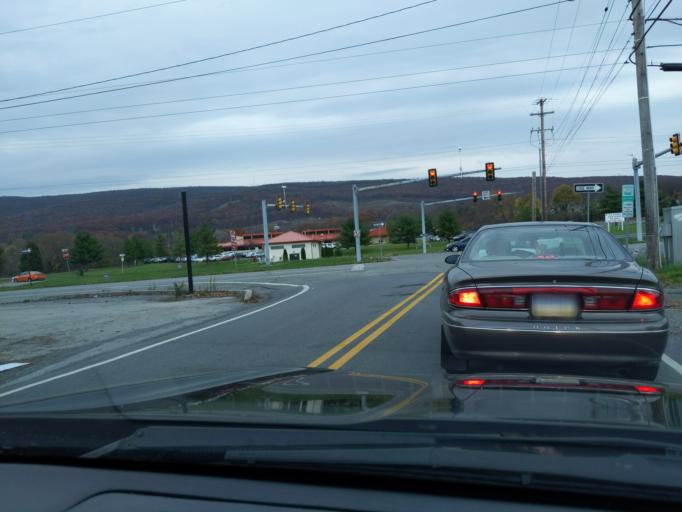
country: US
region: Pennsylvania
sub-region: Blair County
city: Altoona
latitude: 40.4973
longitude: -78.3941
